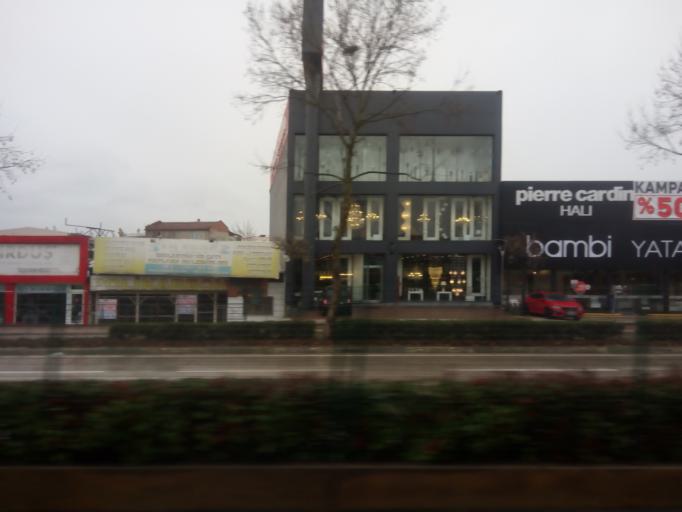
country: TR
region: Bursa
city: Yildirim
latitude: 40.2187
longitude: 28.9985
